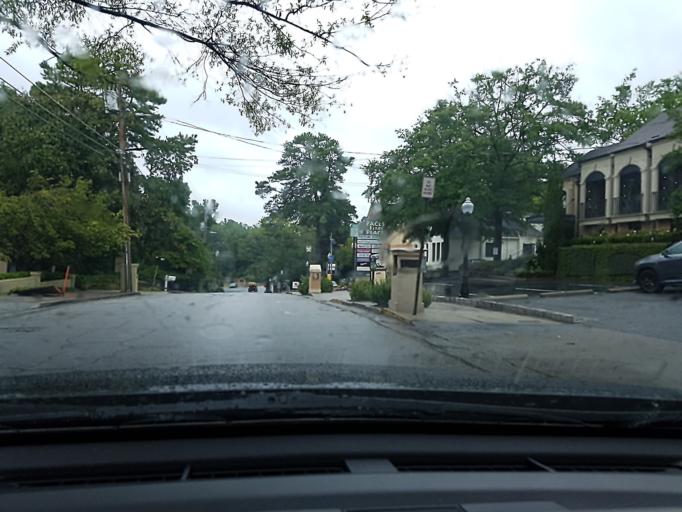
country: US
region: Georgia
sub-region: DeKalb County
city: North Atlanta
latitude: 33.8422
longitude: -84.3819
